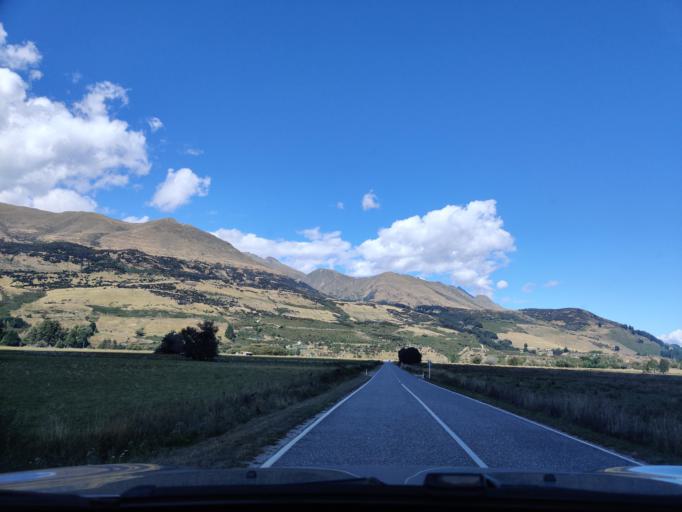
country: NZ
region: Otago
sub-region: Queenstown-Lakes District
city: Queenstown
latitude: -44.7883
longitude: 168.3976
